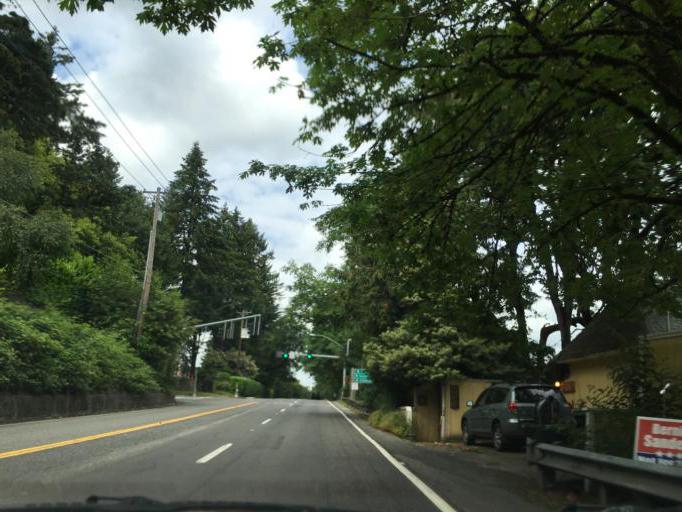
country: US
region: Oregon
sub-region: Clackamas County
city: Milwaukie
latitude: 45.4350
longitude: -122.6537
